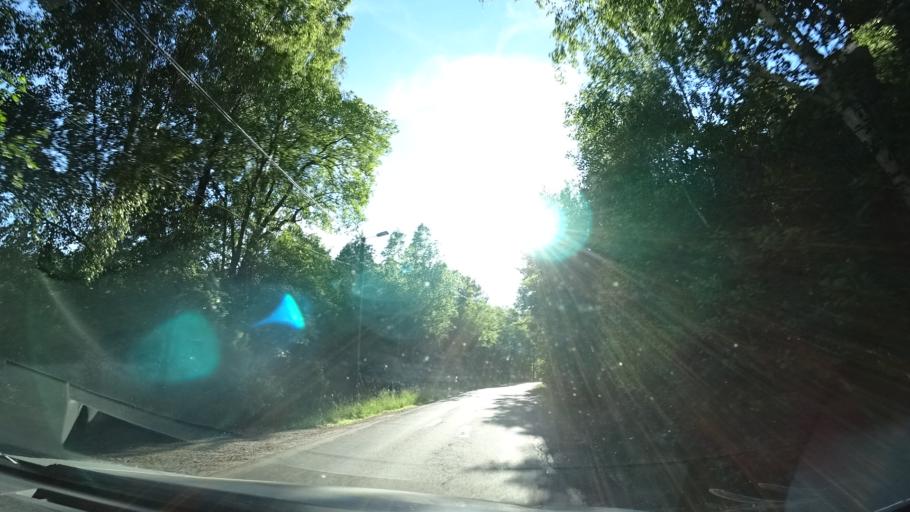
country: SE
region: Vaestra Goetaland
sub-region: Goteborg
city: Billdal
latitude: 57.5879
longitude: 11.9701
